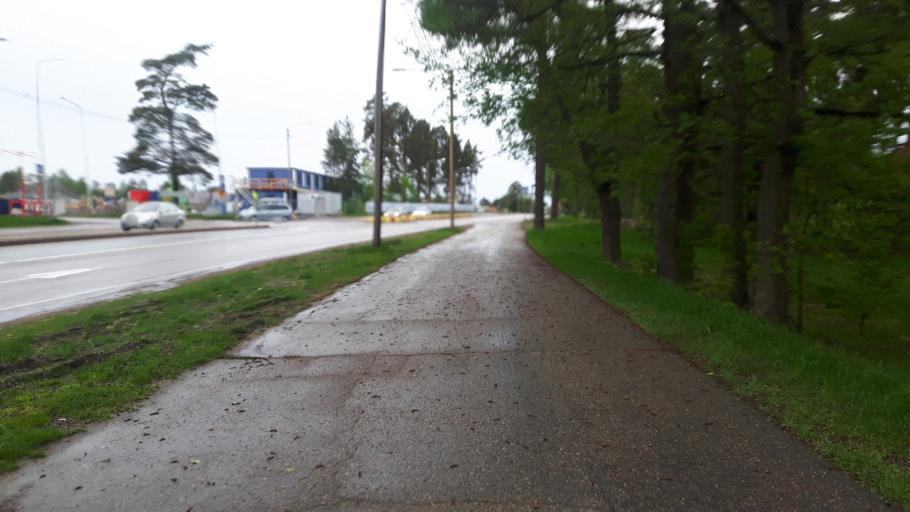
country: FI
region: Kymenlaakso
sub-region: Kotka-Hamina
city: Kotka
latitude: 60.4782
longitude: 26.9138
